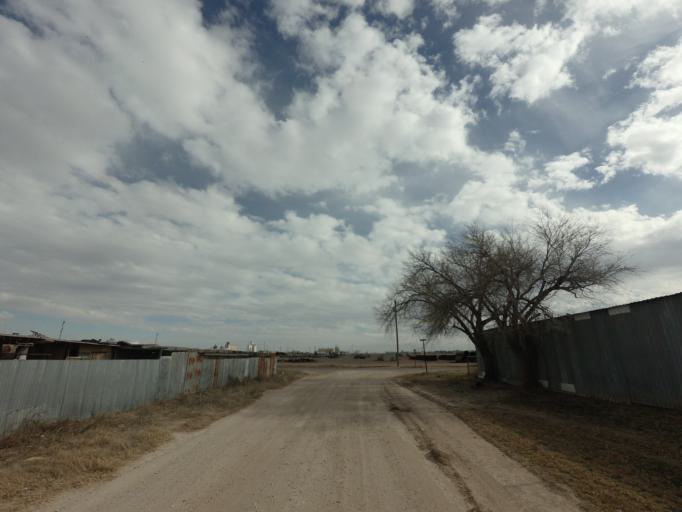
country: US
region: New Mexico
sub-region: Curry County
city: Clovis
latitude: 34.3928
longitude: -103.2145
